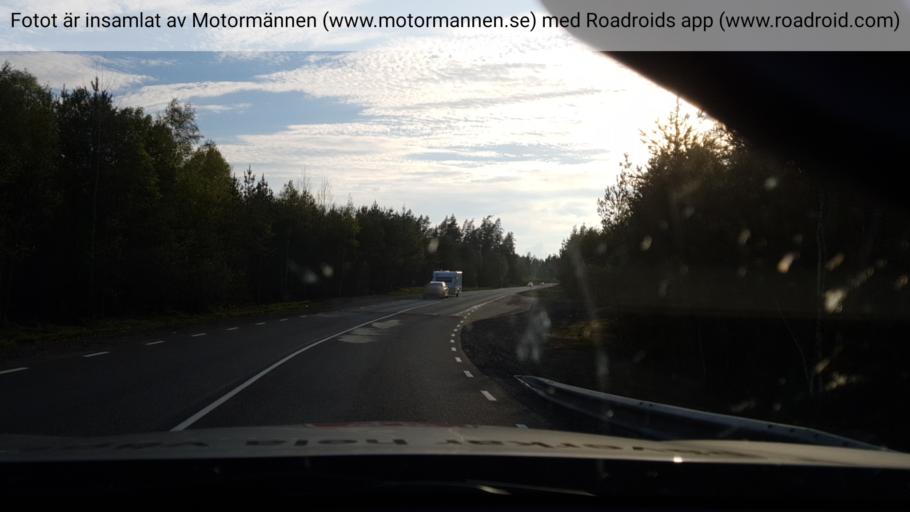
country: SE
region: Joenkoeping
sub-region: Mullsjo Kommun
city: Mullsjoe
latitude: 57.8871
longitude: 13.8942
